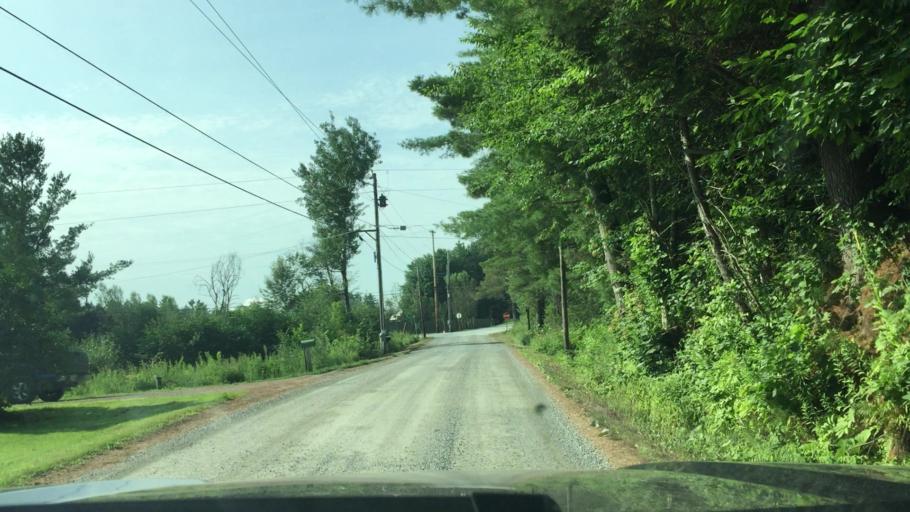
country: US
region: Vermont
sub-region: Chittenden County
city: Milton
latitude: 44.6721
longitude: -72.9742
